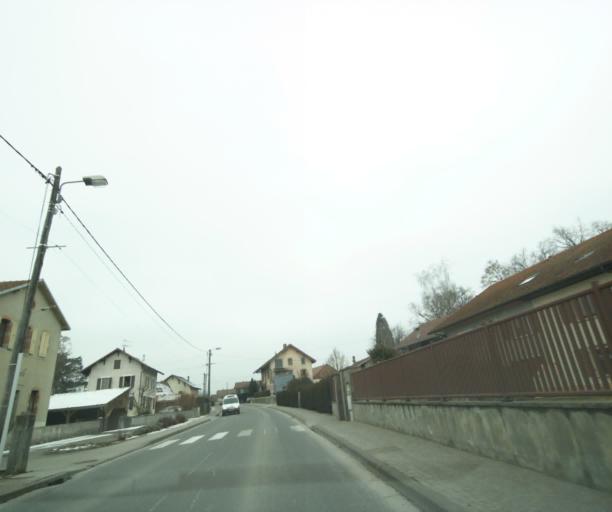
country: FR
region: Rhone-Alpes
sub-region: Departement de la Haute-Savoie
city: Reignier-Esery
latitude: 46.1332
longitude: 6.2953
